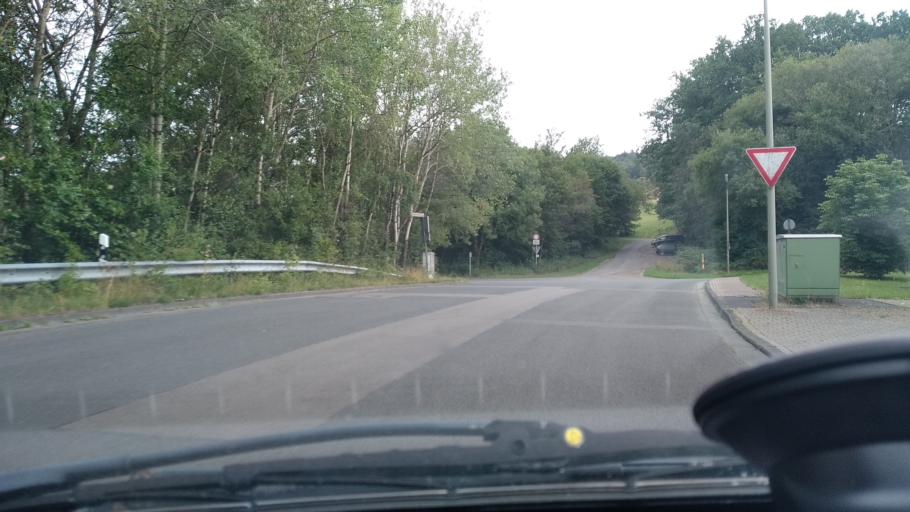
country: DE
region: North Rhine-Westphalia
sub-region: Regierungsbezirk Arnsberg
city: Burbach
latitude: 50.7550
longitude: 8.1144
